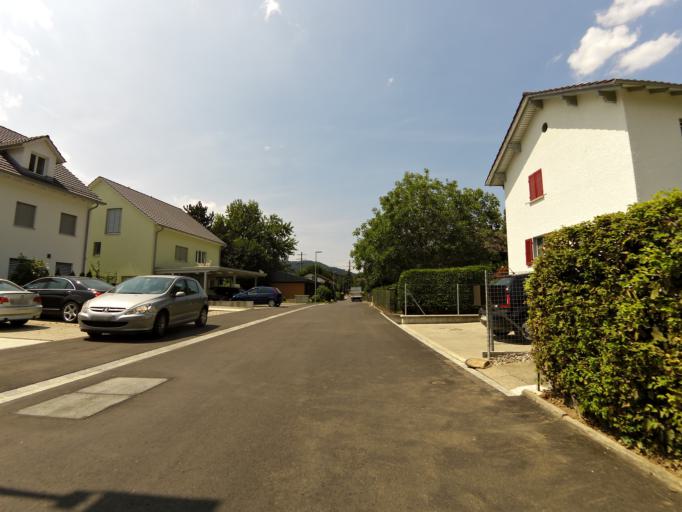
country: CH
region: Aargau
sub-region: Bezirk Baden
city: Killwangen
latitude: 47.4361
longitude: 8.3535
